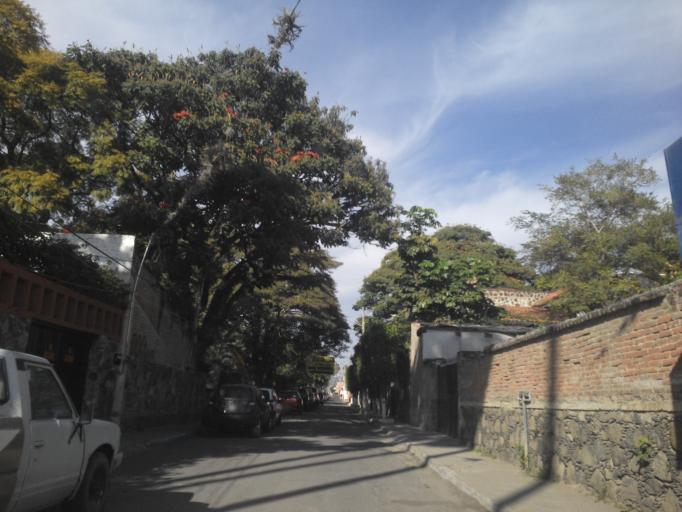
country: MX
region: Jalisco
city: Chapala
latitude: 20.2878
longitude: -103.1914
